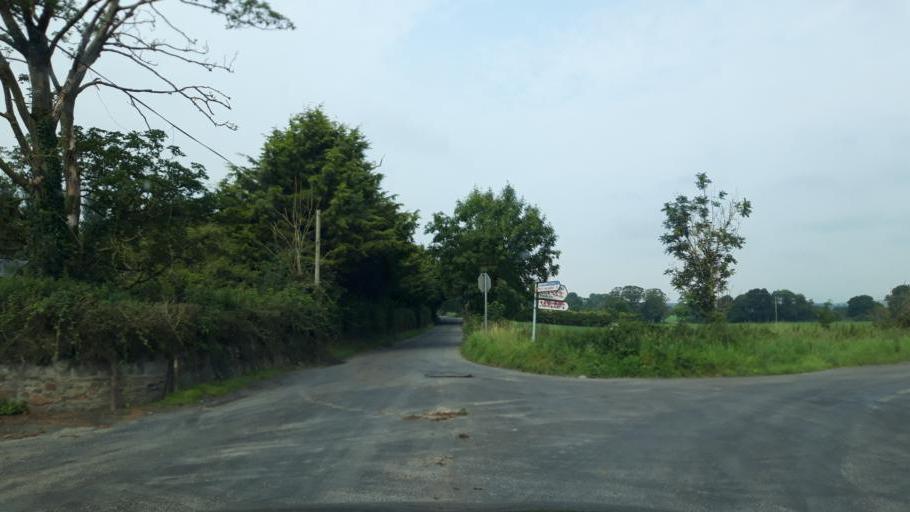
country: IE
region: Munster
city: Fethard
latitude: 52.5579
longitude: -7.5600
